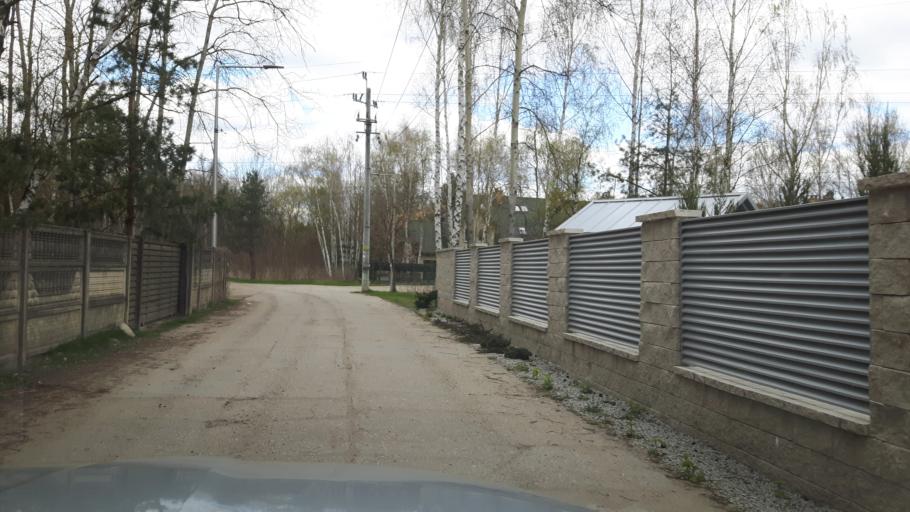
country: PL
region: Masovian Voivodeship
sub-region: Powiat wolominski
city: Kobylka
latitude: 52.3522
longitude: 21.2113
